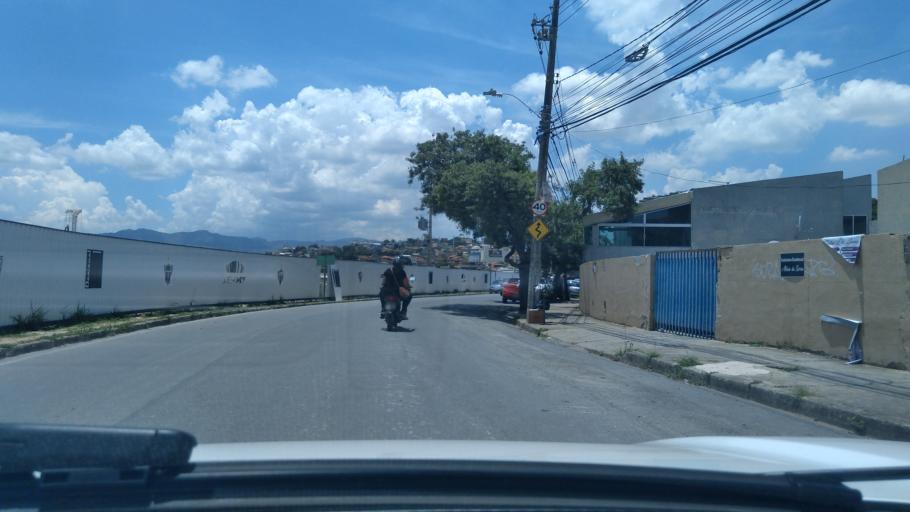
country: BR
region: Minas Gerais
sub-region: Contagem
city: Contagem
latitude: -19.9289
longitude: -44.0163
